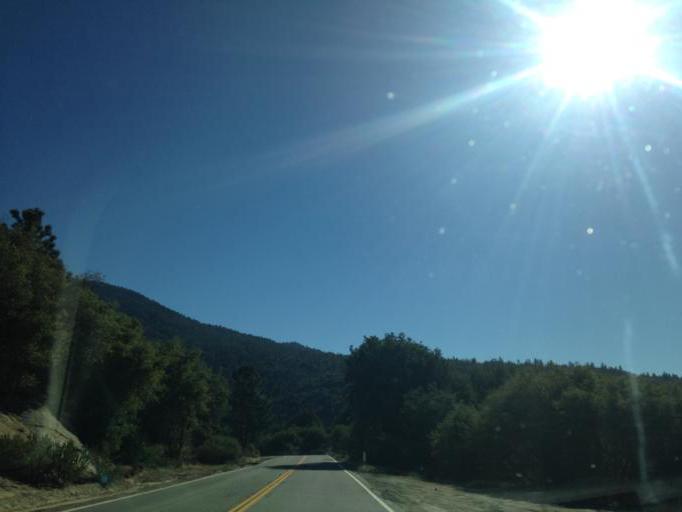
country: US
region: California
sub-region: Riverside County
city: Idyllwild-Pine Cove
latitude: 33.7975
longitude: -116.7593
